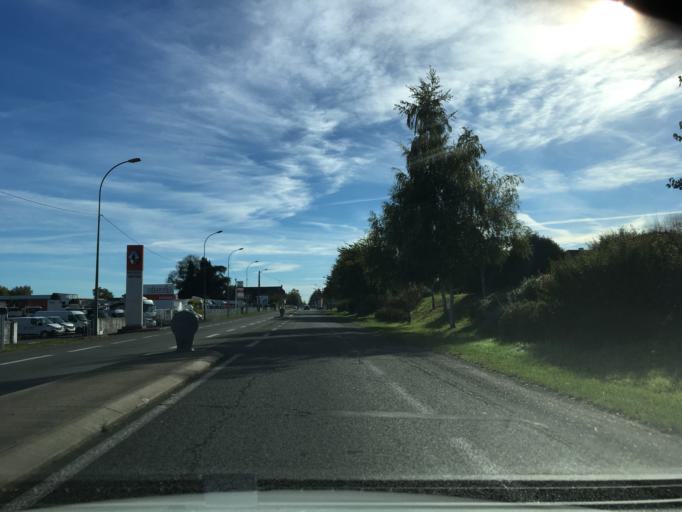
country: FR
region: Aquitaine
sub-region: Departement des Pyrenees-Atlantiques
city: Idron
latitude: 43.3044
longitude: -0.3258
